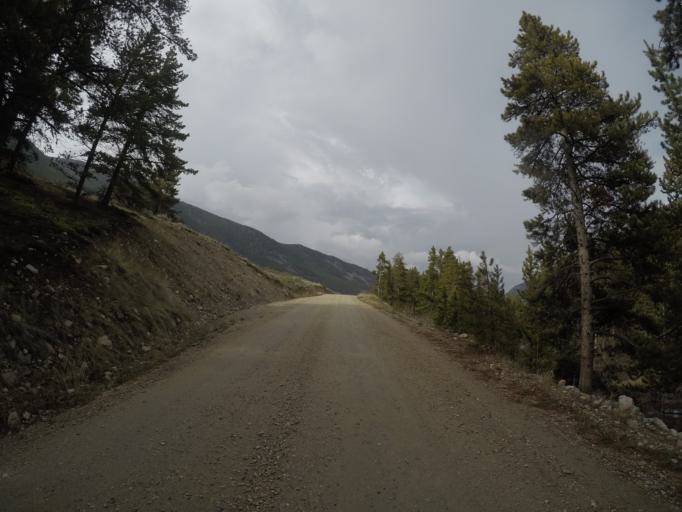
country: US
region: Montana
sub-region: Carbon County
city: Red Lodge
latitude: 45.0502
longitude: -109.4227
